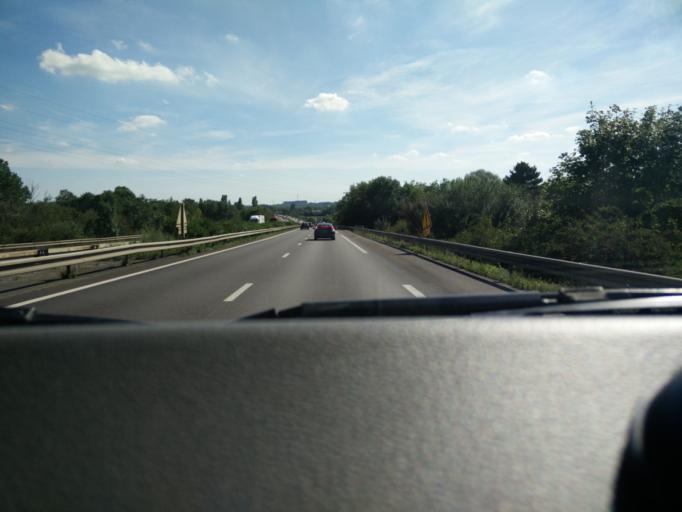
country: FR
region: Lorraine
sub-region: Departement de la Moselle
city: Illange
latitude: 49.3193
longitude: 6.1829
